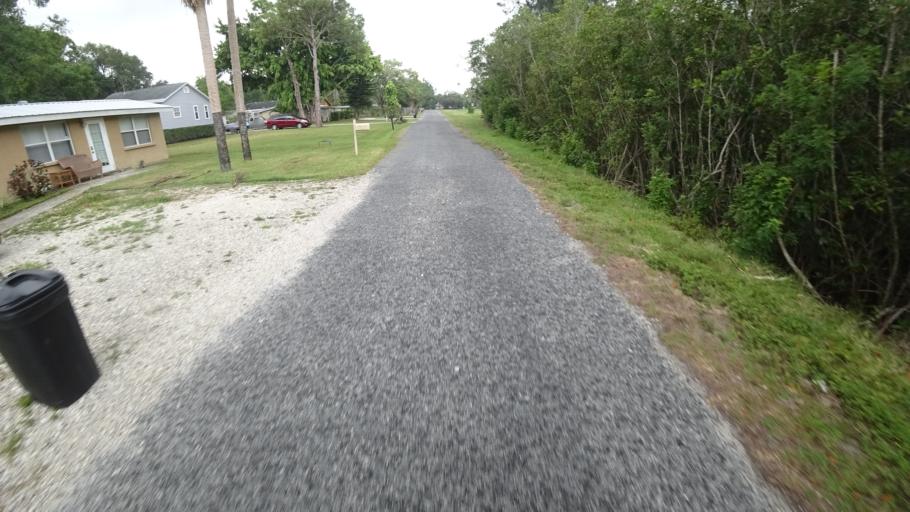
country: US
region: Florida
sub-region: Manatee County
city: Samoset
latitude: 27.4817
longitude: -82.5048
